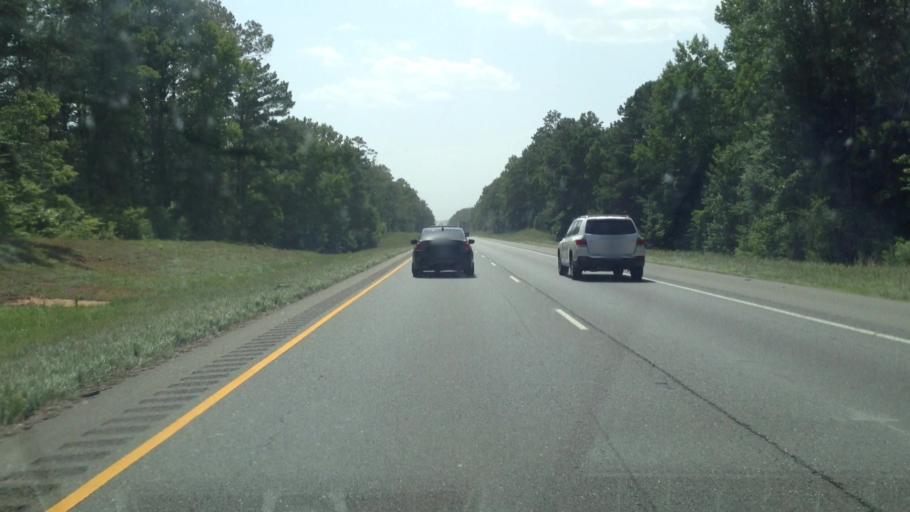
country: US
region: Louisiana
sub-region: Bossier Parish
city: Eastwood
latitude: 32.5423
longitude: -93.5575
